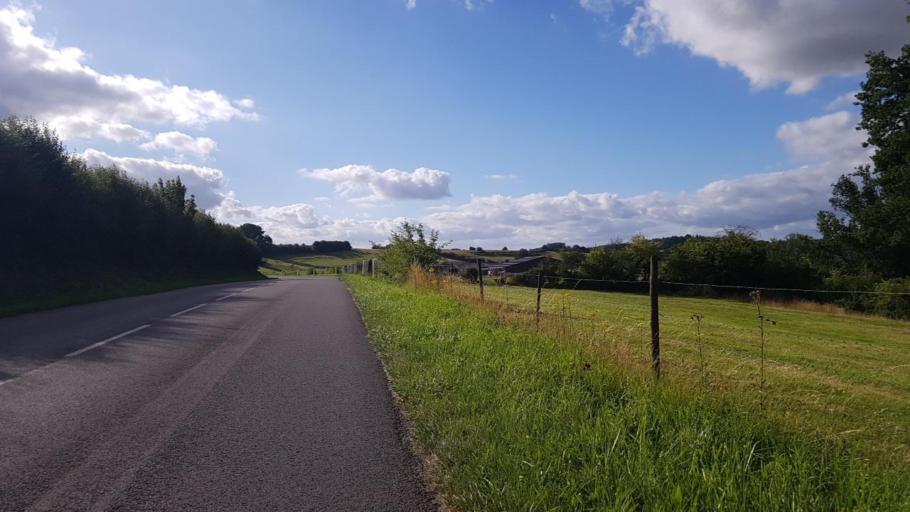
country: FR
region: Picardie
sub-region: Departement de l'Aisne
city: Hirson
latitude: 49.9215
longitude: 4.0523
